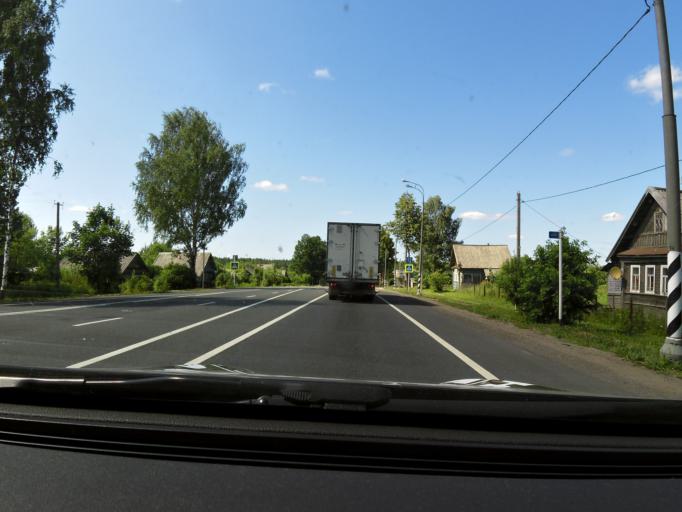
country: RU
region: Novgorod
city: Kresttsy
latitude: 58.1720
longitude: 32.7073
